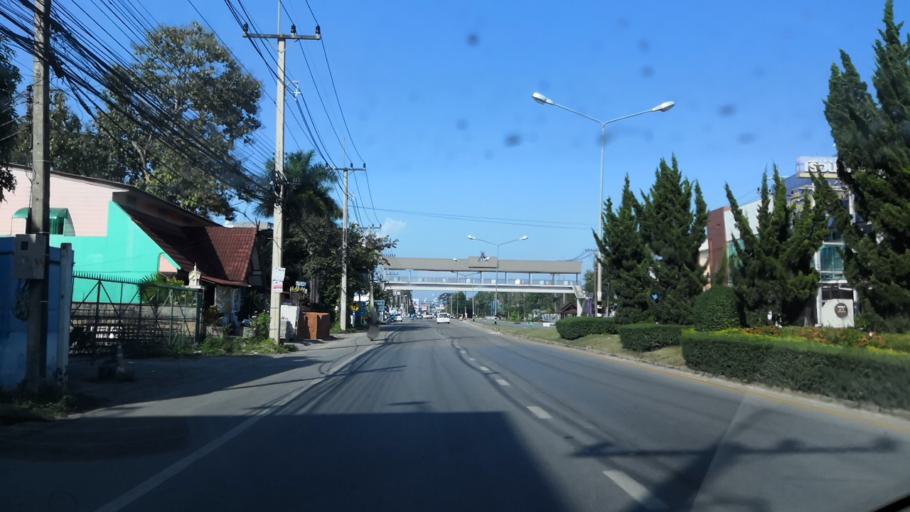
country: TH
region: Chiang Rai
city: Chiang Rai
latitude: 19.9341
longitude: 99.8448
